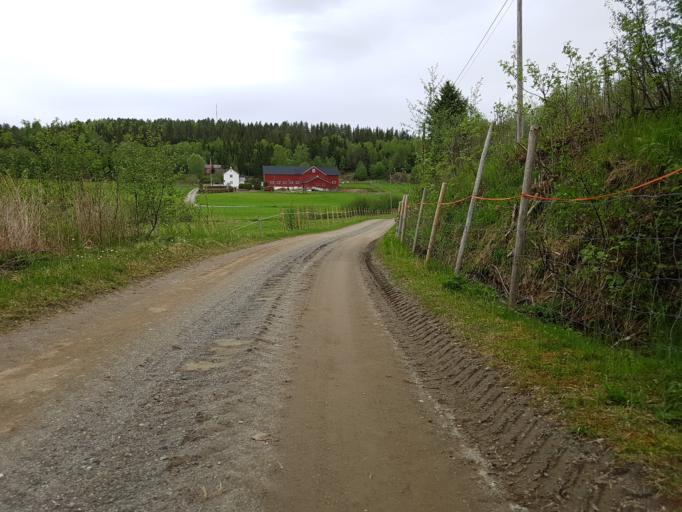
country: NO
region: Nord-Trondelag
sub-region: Levanger
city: Skogn
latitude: 63.6293
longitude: 11.2668
